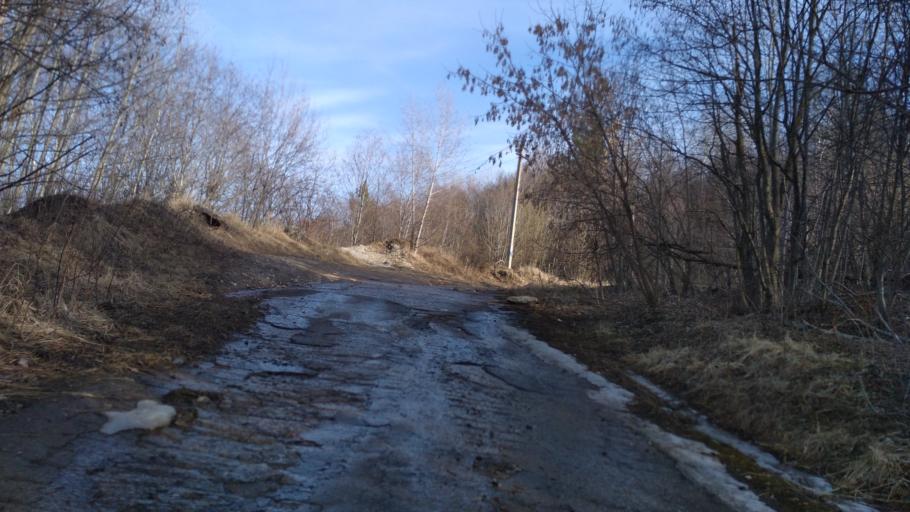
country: RU
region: Chuvashia
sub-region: Cheboksarskiy Rayon
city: Cheboksary
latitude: 56.1439
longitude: 47.3264
